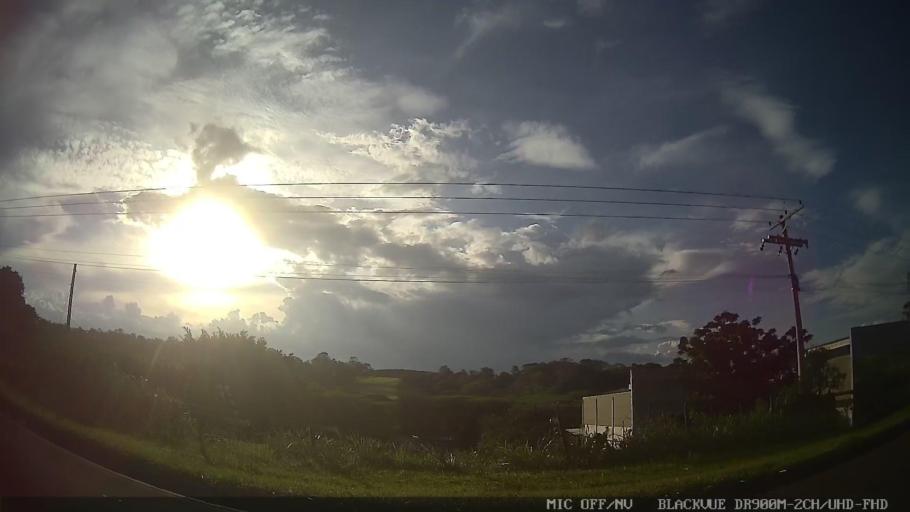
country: BR
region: Sao Paulo
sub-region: Tiete
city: Tiete
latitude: -23.0934
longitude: -47.7226
